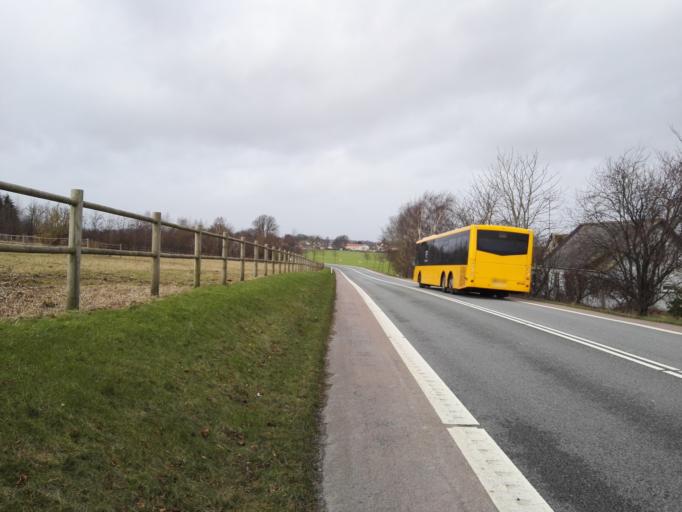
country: DK
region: Capital Region
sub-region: Frederikssund Kommune
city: Skibby
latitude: 55.6796
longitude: 11.9273
